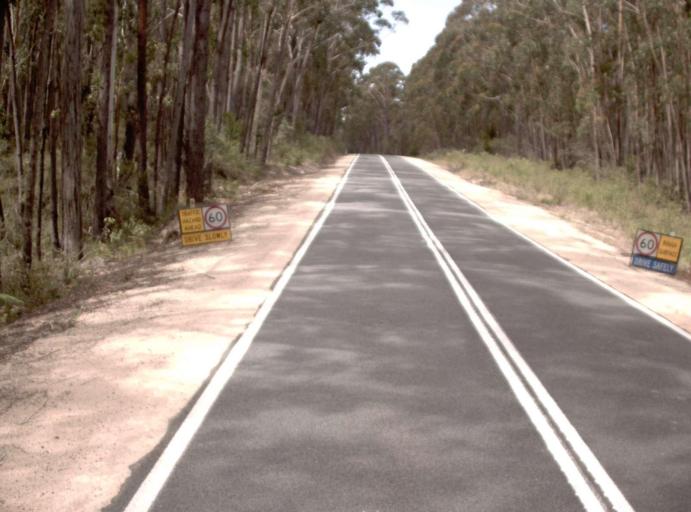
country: AU
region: New South Wales
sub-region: Bega Valley
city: Eden
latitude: -37.4997
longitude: 149.5419
